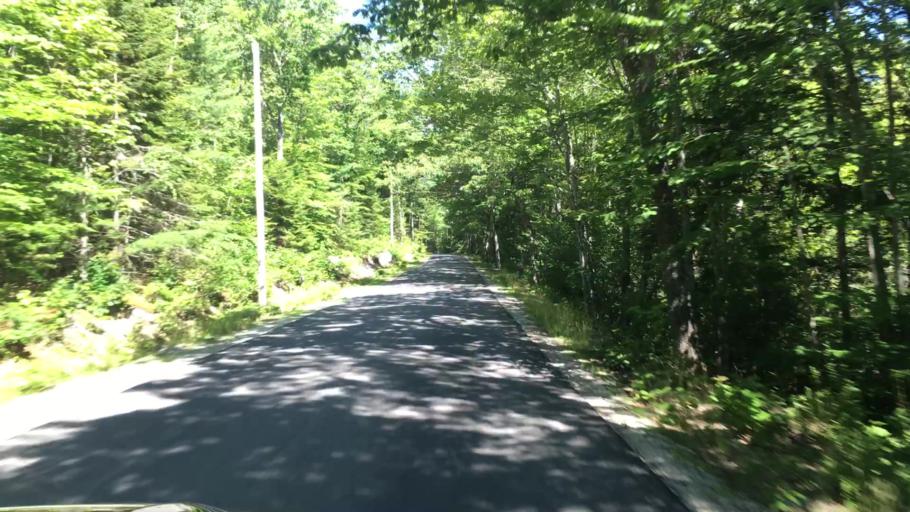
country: US
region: Maine
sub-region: Hancock County
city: Sedgwick
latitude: 44.3350
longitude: -68.6612
